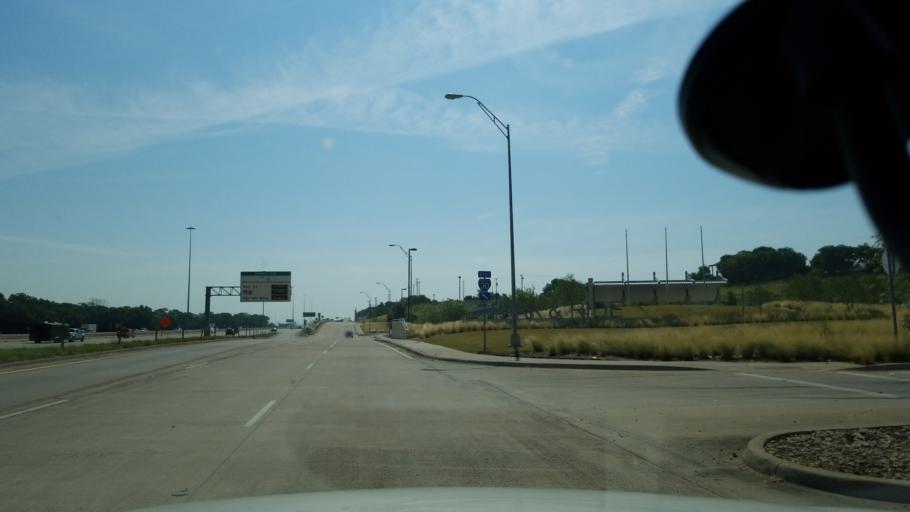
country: US
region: Texas
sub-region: Dallas County
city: Grand Prairie
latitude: 32.7582
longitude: -96.9895
